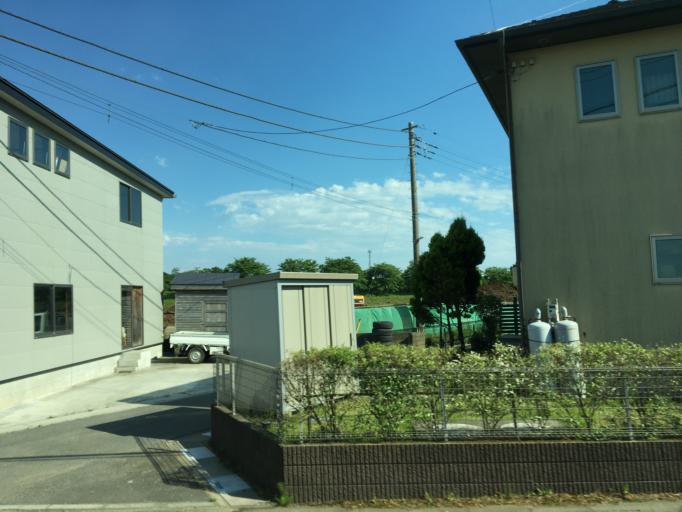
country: JP
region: Saitama
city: Sakado
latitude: 35.9600
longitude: 139.3762
